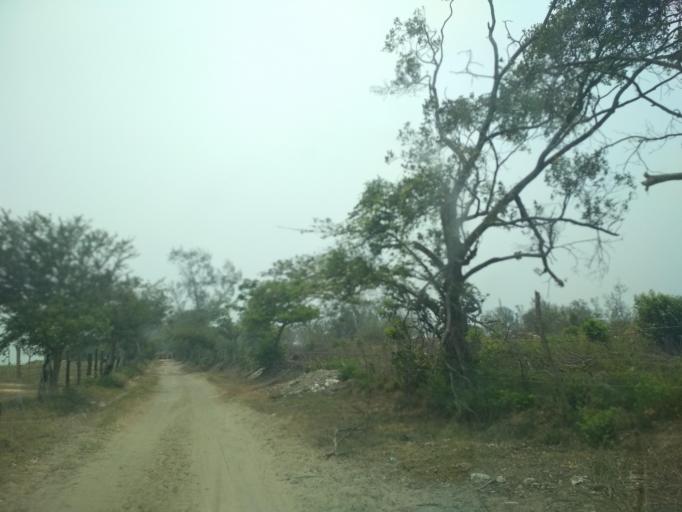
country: MX
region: Veracruz
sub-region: Veracruz
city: Las Amapolas
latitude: 19.1473
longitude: -96.2086
